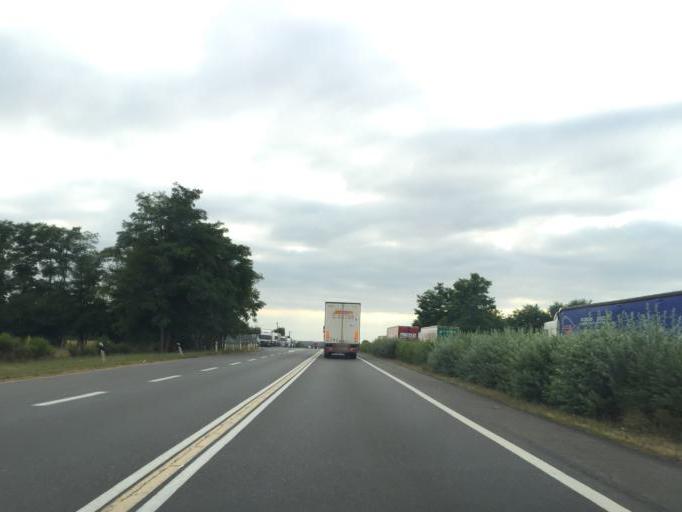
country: FR
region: Auvergne
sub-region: Departement de l'Allier
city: Beaulon
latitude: 46.5345
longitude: 3.5921
